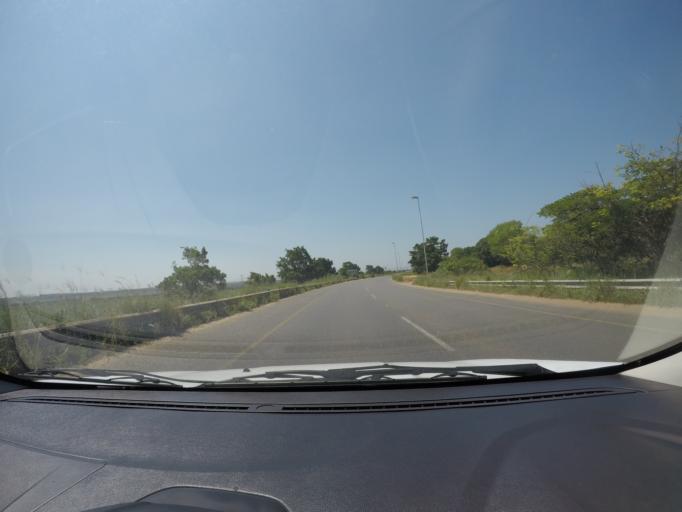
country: ZA
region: KwaZulu-Natal
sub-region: uThungulu District Municipality
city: Empangeni
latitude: -28.7780
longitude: 31.9581
